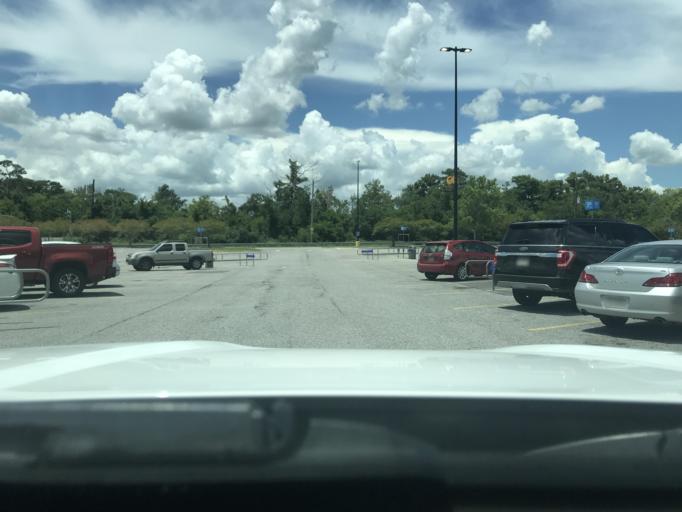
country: US
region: Louisiana
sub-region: Calcasieu Parish
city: Moss Bluff
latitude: 30.2700
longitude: -93.1802
